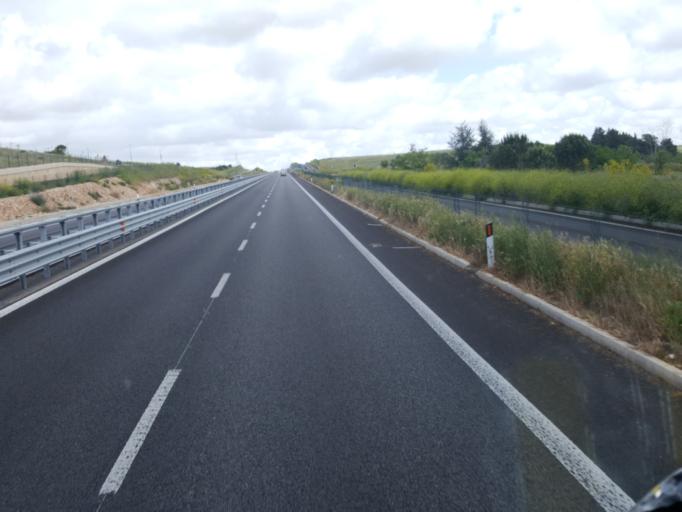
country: IT
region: Apulia
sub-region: Provincia di Bari
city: Altamura
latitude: 40.8647
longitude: 16.5995
